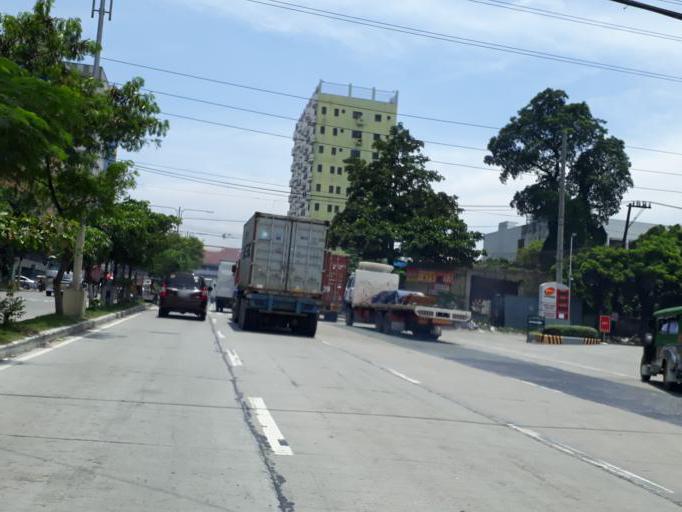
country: PH
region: Metro Manila
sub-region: Caloocan City
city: Niugan
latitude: 14.6446
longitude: 120.9816
